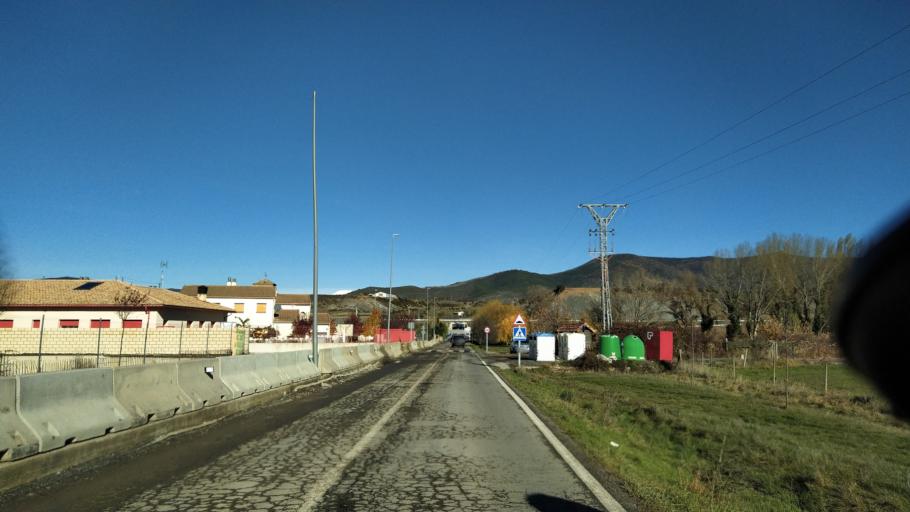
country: ES
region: Aragon
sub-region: Provincia de Huesca
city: Santa Cruz de la Seros
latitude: 42.5594
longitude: -0.7128
